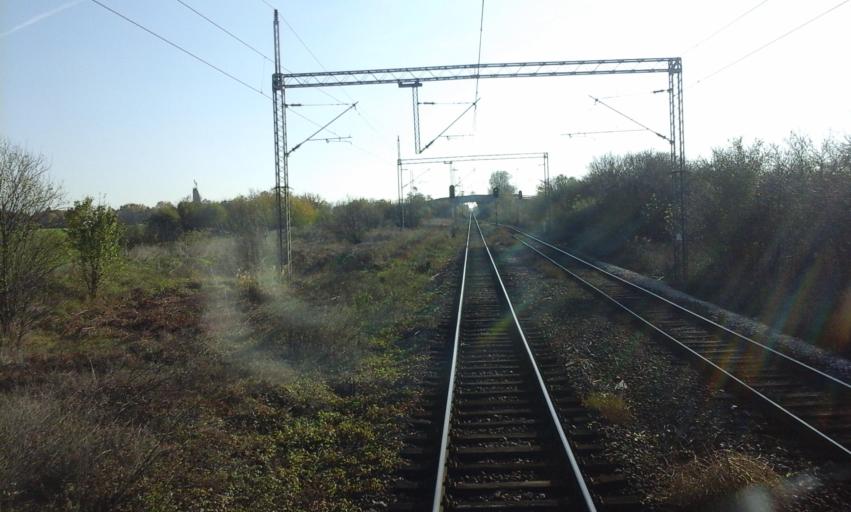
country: RS
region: Autonomna Pokrajina Vojvodina
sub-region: Severnobacki Okrug
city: Mali Igos
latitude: 45.7445
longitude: 19.6489
